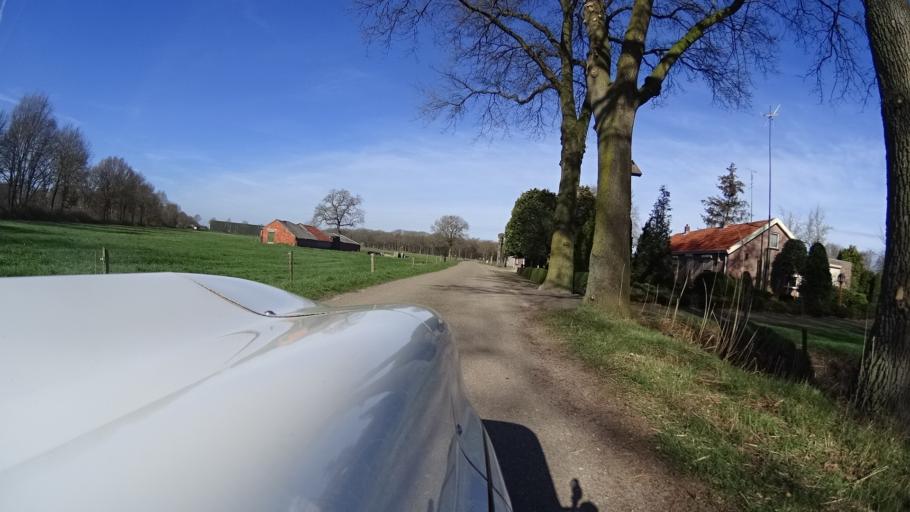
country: NL
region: North Brabant
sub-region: Gemeente Landerd
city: Zeeland
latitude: 51.6651
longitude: 5.6783
